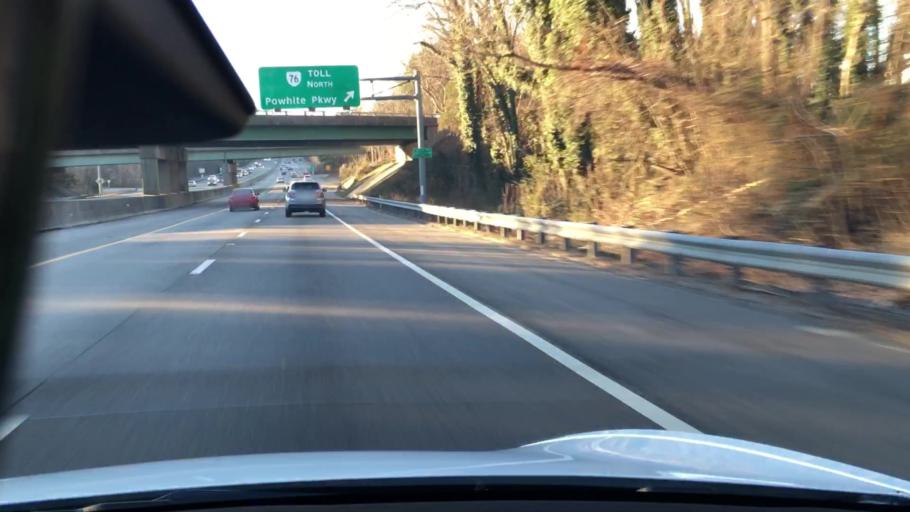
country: US
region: Virginia
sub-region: Chesterfield County
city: Bon Air
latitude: 37.5269
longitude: -77.5287
